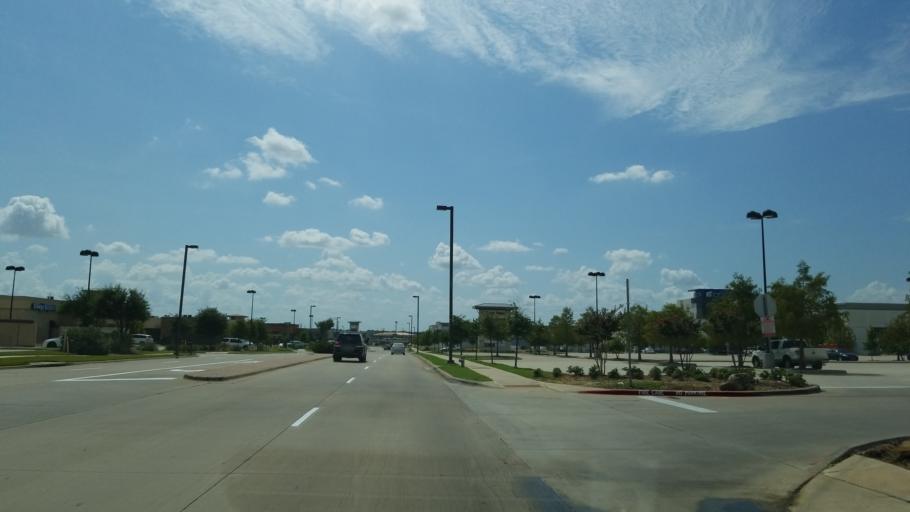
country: US
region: Texas
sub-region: Tarrant County
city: Euless
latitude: 32.8770
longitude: -97.1018
